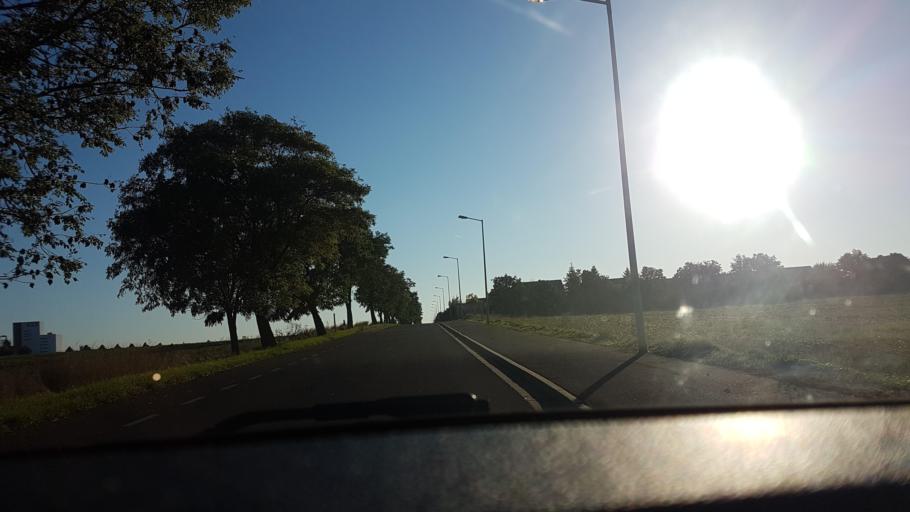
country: DE
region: Saxony-Anhalt
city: Bernburg
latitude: 51.7831
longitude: 11.7254
